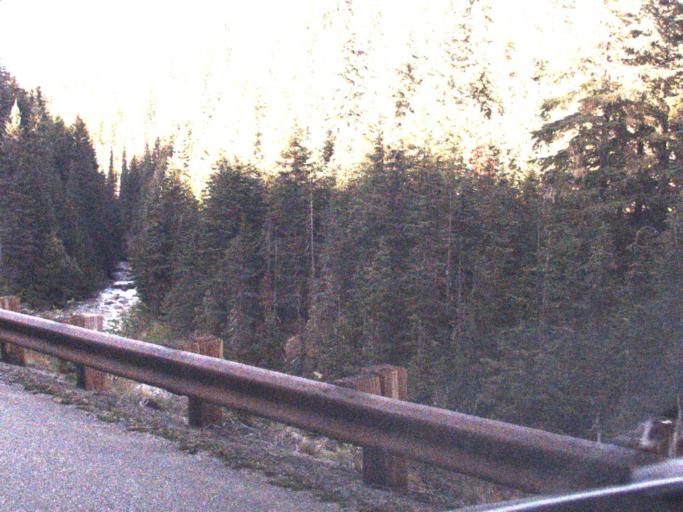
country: US
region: Washington
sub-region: Snohomish County
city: Darrington
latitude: 48.6296
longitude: -120.8445
